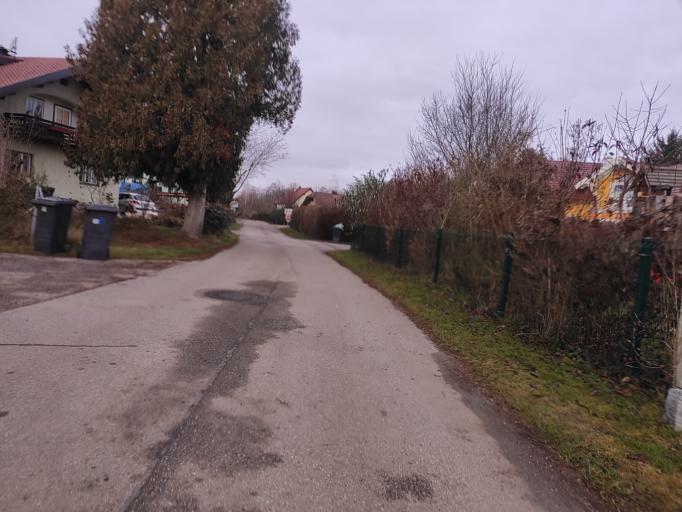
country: AT
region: Salzburg
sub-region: Politischer Bezirk Salzburg-Umgebung
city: Strasswalchen
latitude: 47.9908
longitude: 13.2404
